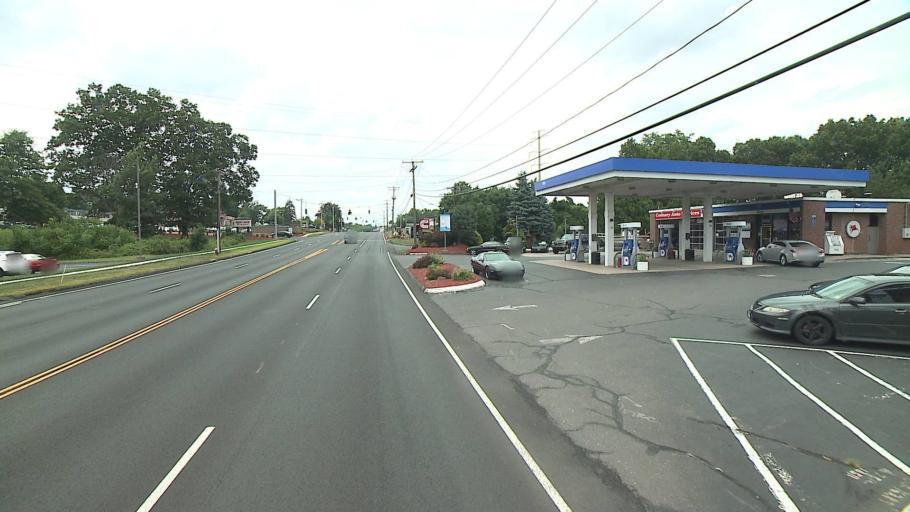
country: US
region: Connecticut
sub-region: Middlesex County
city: Cromwell
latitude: 41.6454
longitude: -72.6777
